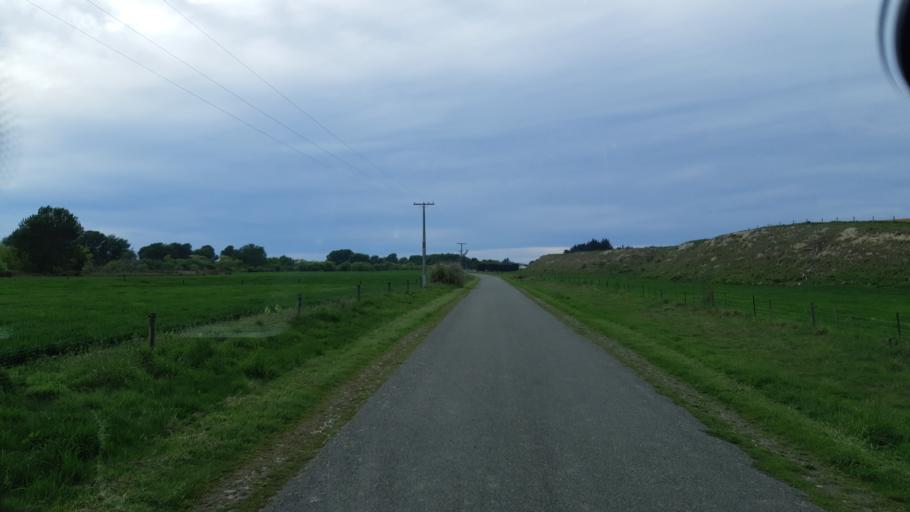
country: NZ
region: Canterbury
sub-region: Timaru District
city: Timaru
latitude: -44.5398
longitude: 171.1555
